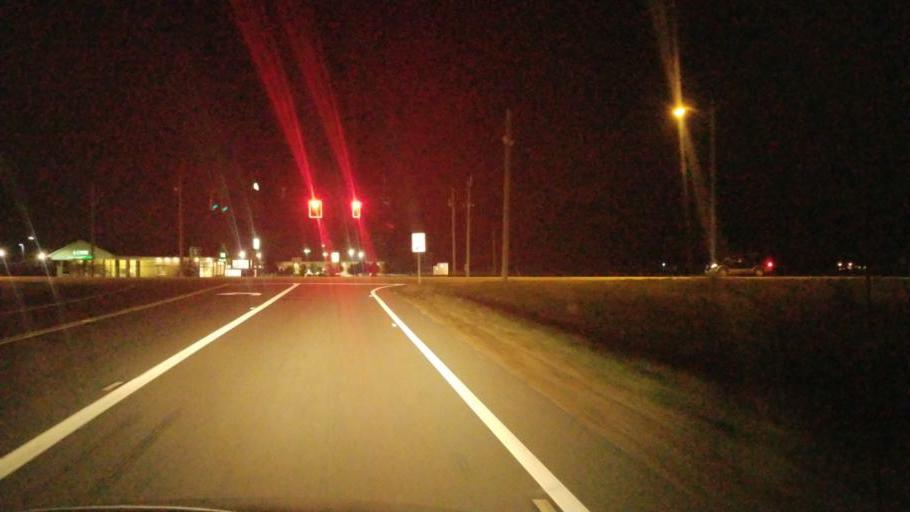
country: US
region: Ohio
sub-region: Fayette County
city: Washington Court House
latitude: 39.5230
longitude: -83.4629
